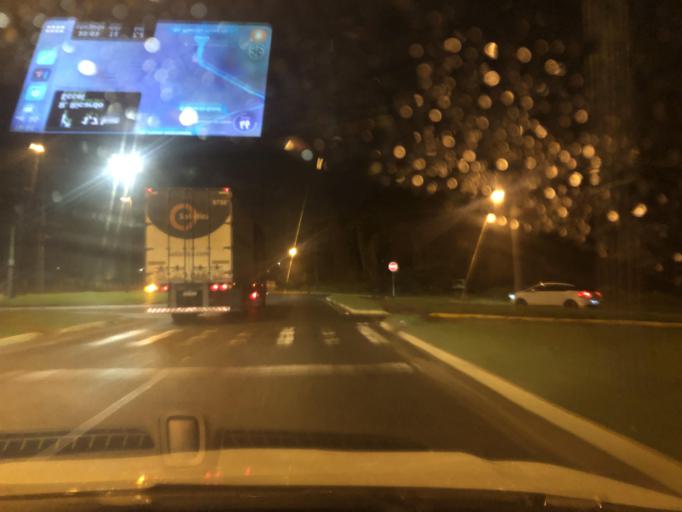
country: BR
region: Santa Catarina
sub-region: Joinville
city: Joinville
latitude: -26.3784
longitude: -48.8432
